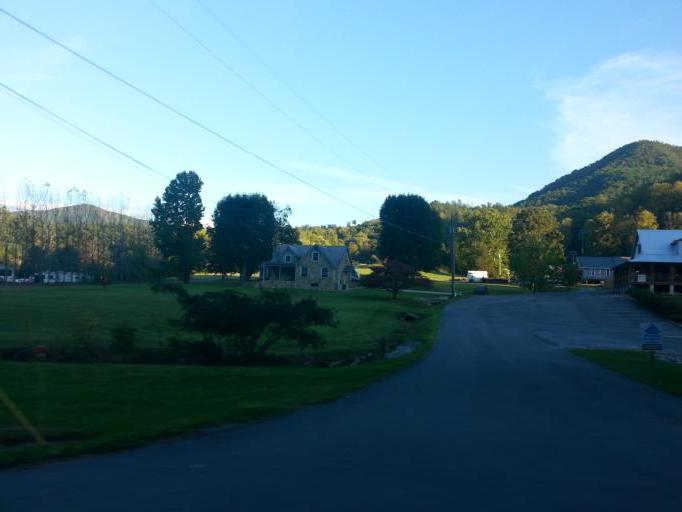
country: US
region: Tennessee
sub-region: Sevier County
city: Pigeon Forge
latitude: 35.7044
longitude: -83.6721
